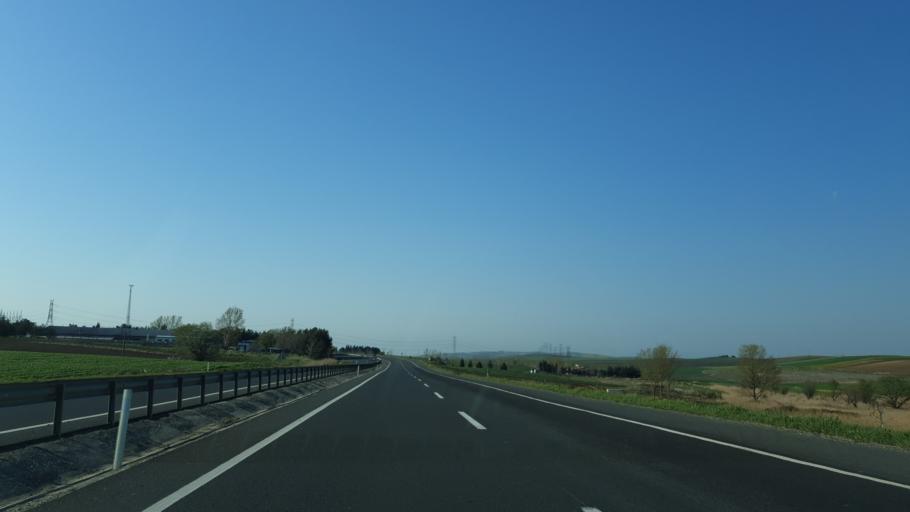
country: TR
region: Tekirdag
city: Corlu
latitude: 41.1161
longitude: 27.7491
